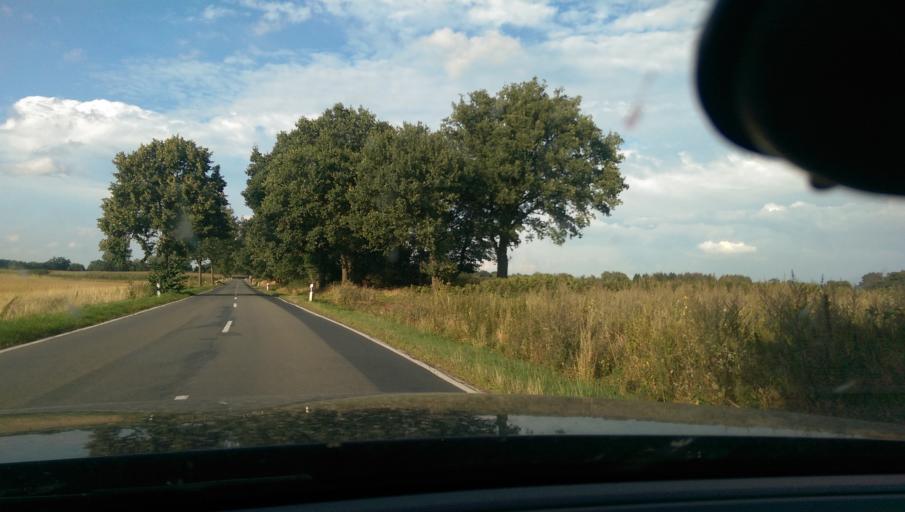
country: DE
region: Lower Saxony
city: Neustadt am Rubenberge
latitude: 52.5681
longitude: 9.5552
